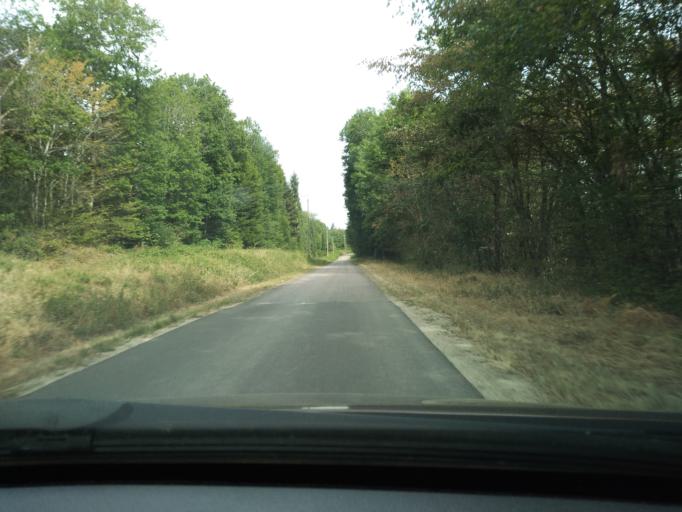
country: FR
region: Bourgogne
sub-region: Departement de la Cote-d'Or
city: Saulieu
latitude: 47.3775
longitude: 4.0786
